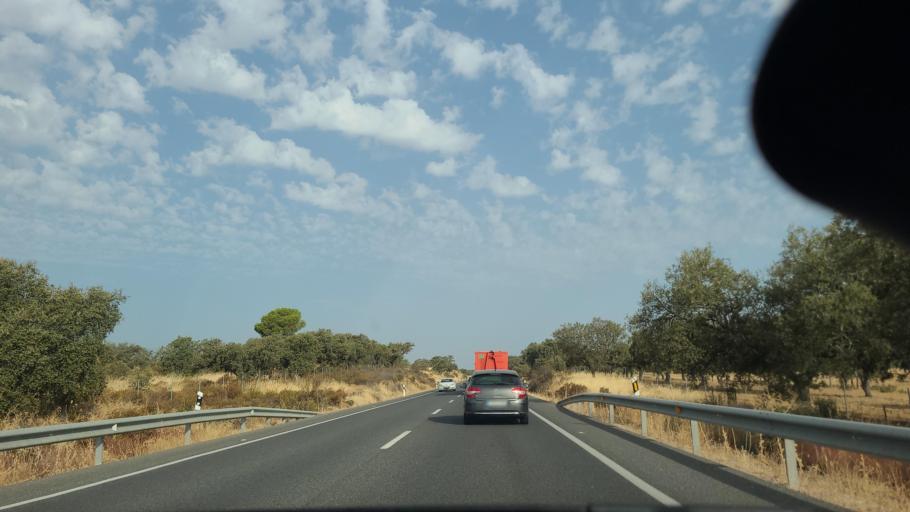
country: ES
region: Andalusia
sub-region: Province of Cordoba
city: Obejo
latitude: 38.0664
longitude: -4.8308
